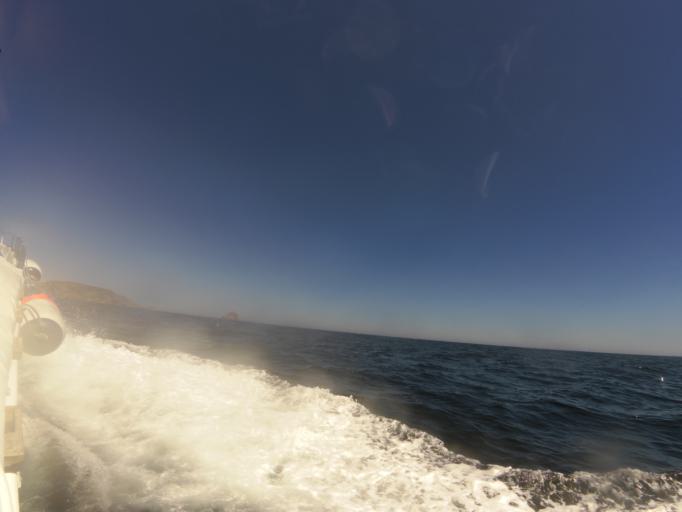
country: PT
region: Leiria
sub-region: Peniche
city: Peniche
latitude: 39.4029
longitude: -9.4912
